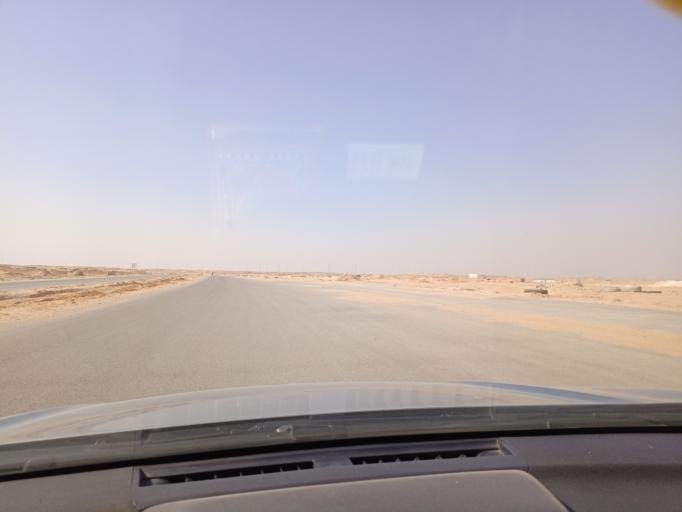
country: EG
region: Muhafazat al Qalyubiyah
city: Al Khankah
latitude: 30.0400
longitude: 31.7155
